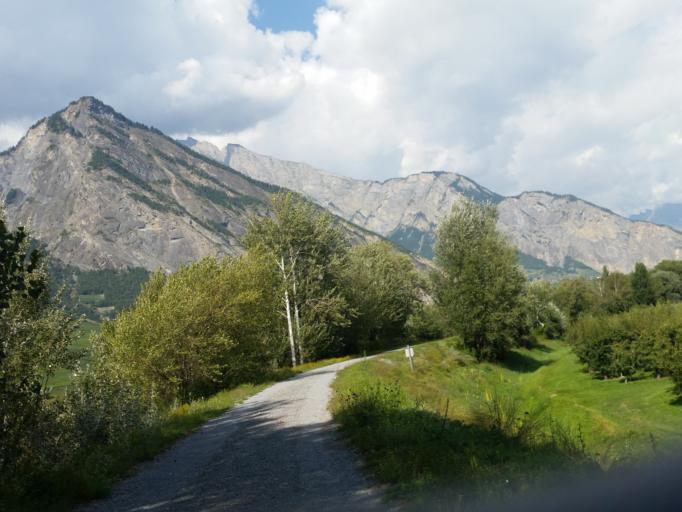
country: CH
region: Valais
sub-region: Martigny District
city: Leytron
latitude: 46.1731
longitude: 7.2012
